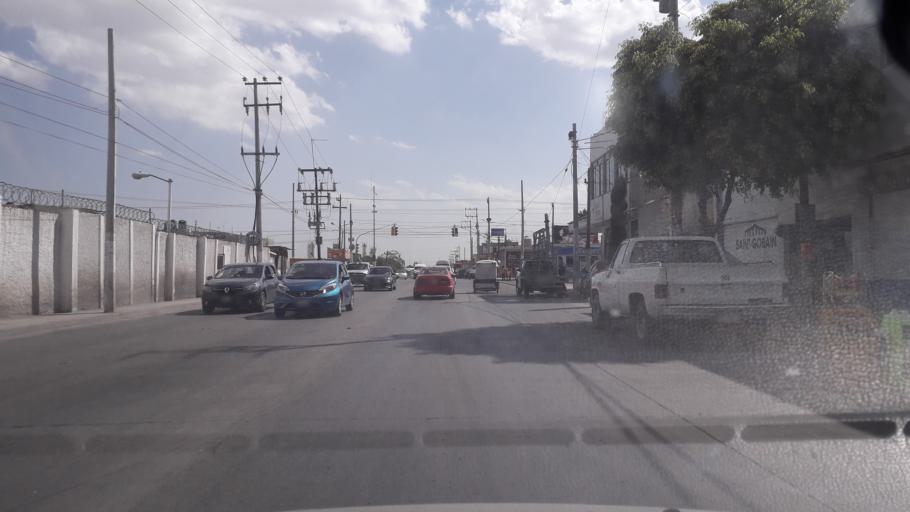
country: MX
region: Mexico
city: Ecatepec
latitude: 19.6249
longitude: -99.0486
